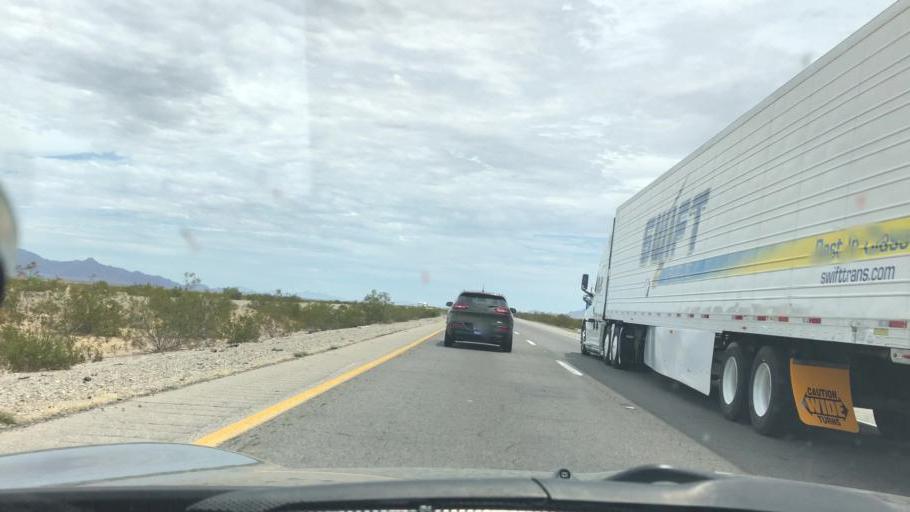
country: US
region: California
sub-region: Riverside County
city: Mesa Verde
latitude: 33.6256
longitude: -115.0551
